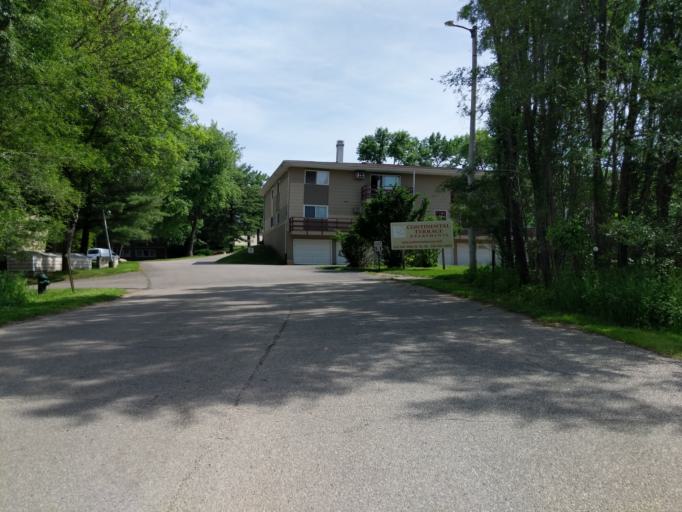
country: US
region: Iowa
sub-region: Linn County
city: Cedar Rapids
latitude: 42.0160
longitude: -91.6310
